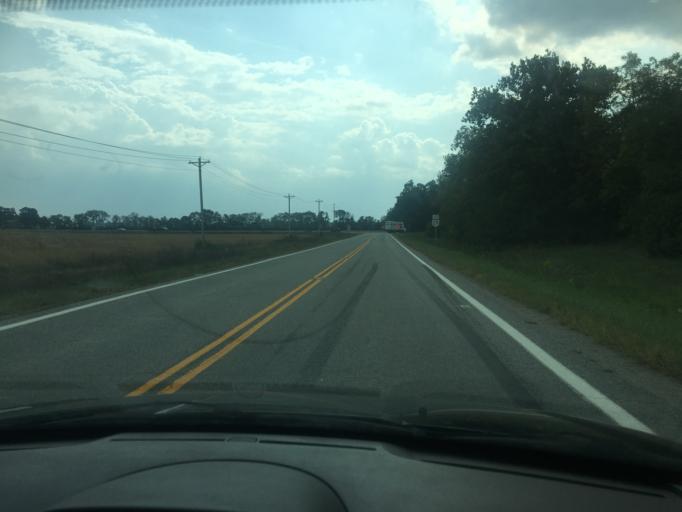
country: US
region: Ohio
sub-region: Champaign County
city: Urbana
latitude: 40.1561
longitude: -83.7866
